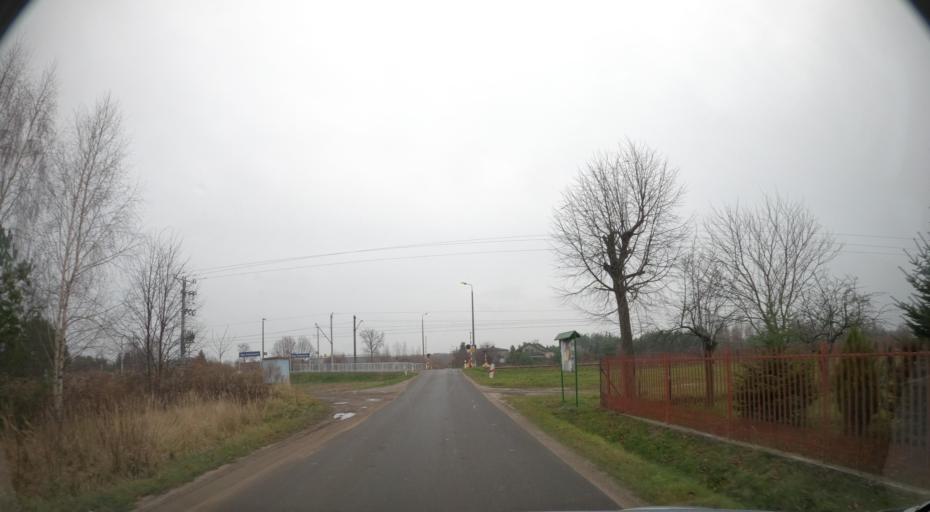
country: PL
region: Masovian Voivodeship
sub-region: Powiat radomski
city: Jastrzebia
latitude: 51.4149
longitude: 21.2514
